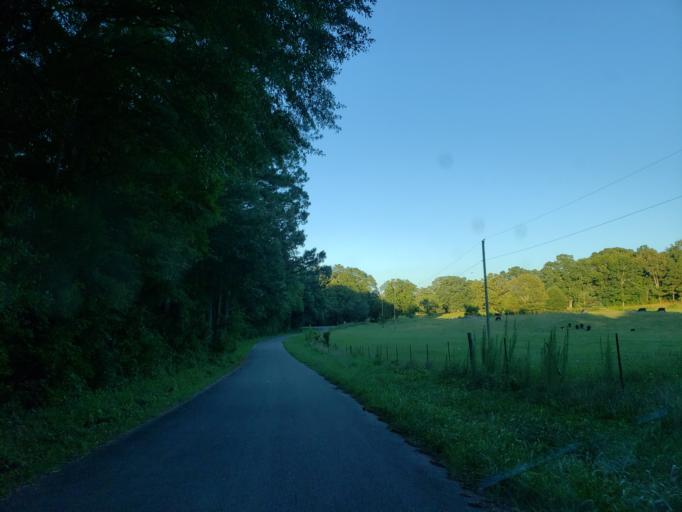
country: US
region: Georgia
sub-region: Bartow County
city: Euharlee
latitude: 34.0809
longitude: -84.9123
